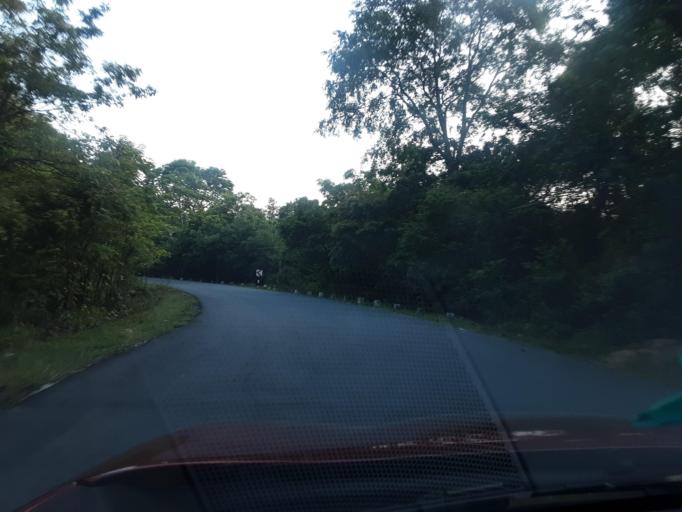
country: LK
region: Central
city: Dambulla
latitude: 7.8120
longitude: 80.7672
